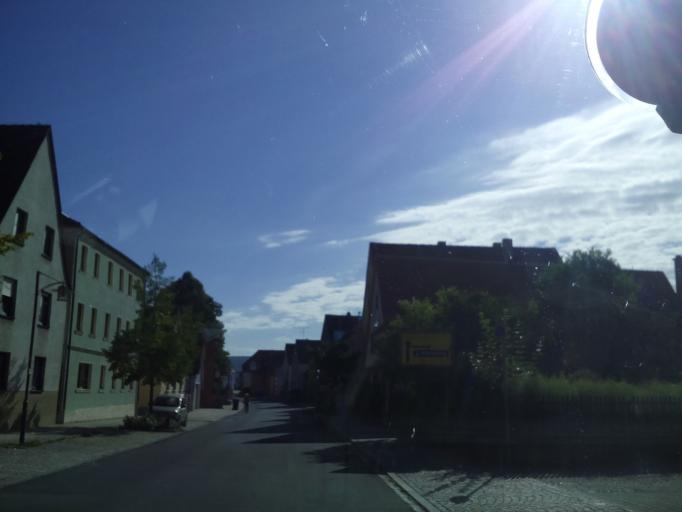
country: DE
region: Bavaria
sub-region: Upper Franconia
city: Buttenheim
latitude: 49.8028
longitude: 11.0309
